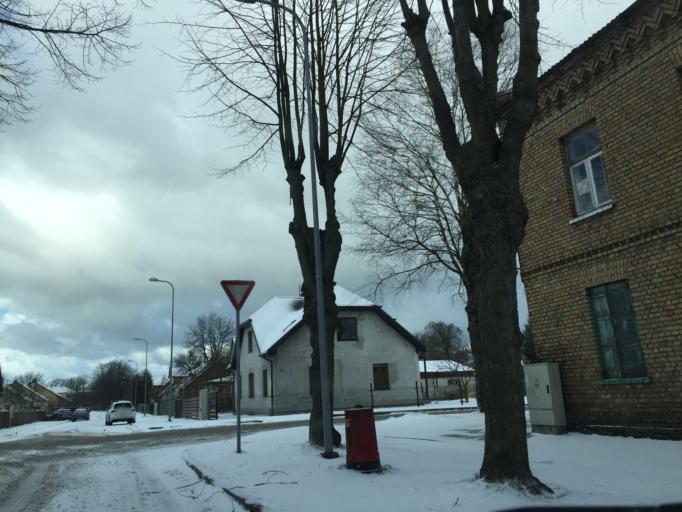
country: LV
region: Ventspils
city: Ventspils
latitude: 57.3842
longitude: 21.5644
